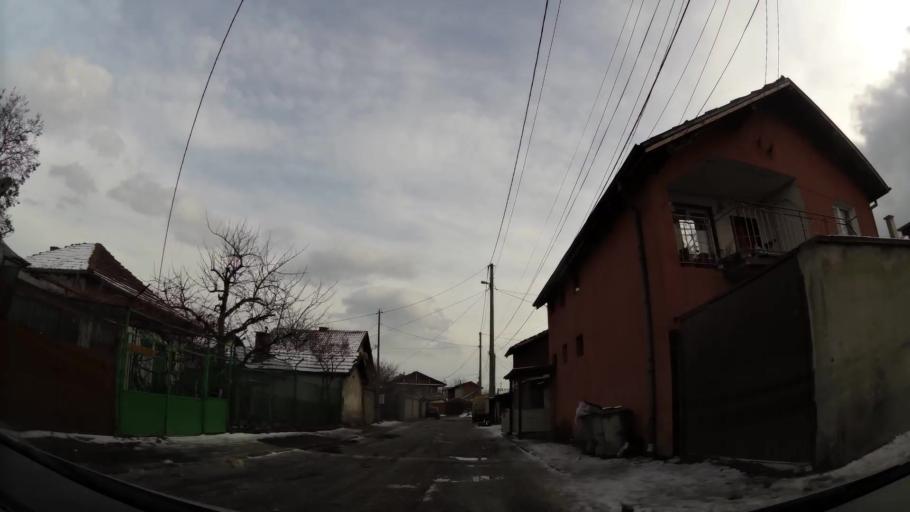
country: BG
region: Sofia-Capital
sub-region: Stolichna Obshtina
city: Sofia
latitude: 42.6875
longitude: 23.3856
